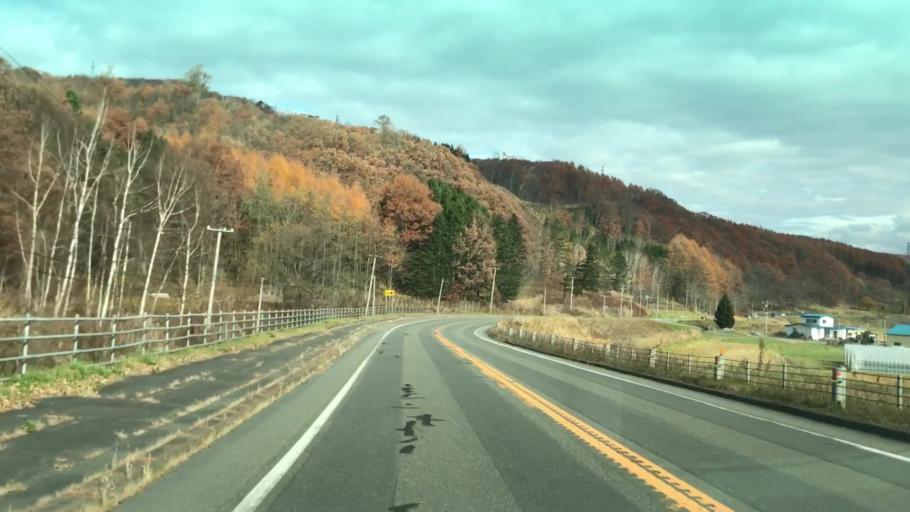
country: JP
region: Hokkaido
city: Shizunai-furukawacho
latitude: 42.7184
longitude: 142.2664
